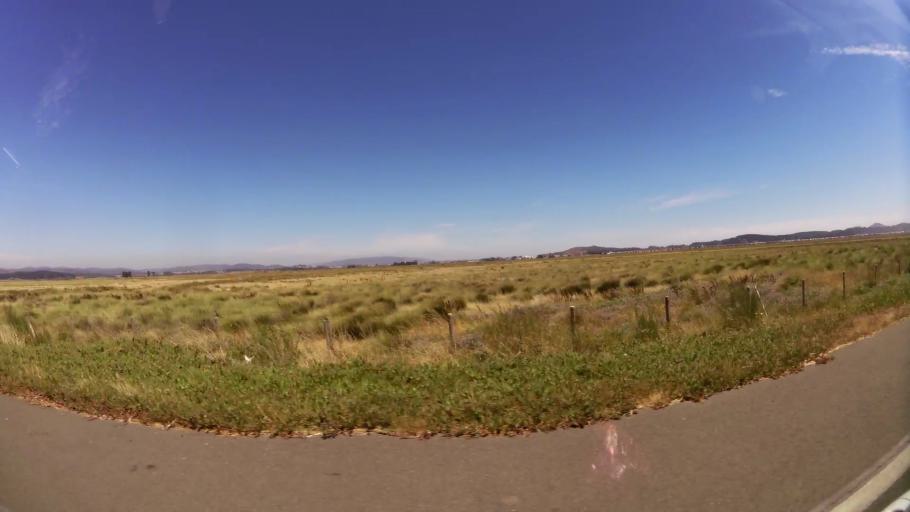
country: CL
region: Biobio
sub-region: Provincia de Concepcion
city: Talcahuano
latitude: -36.7342
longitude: -73.0658
